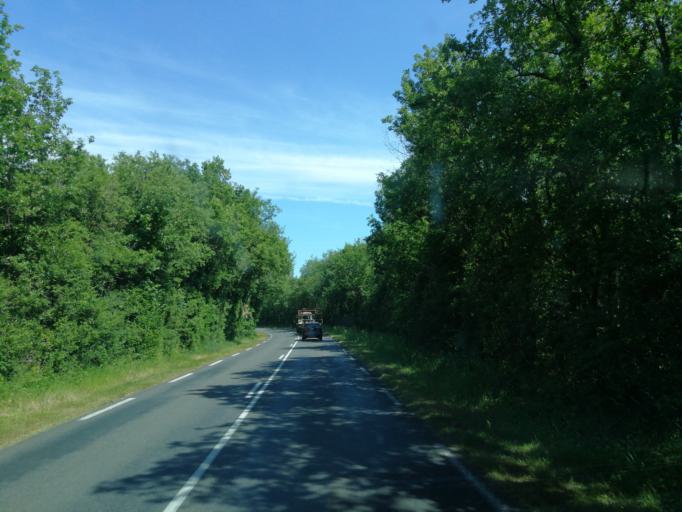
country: FR
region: Poitou-Charentes
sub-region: Departement des Deux-Sevres
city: Saint-Jean-de-Thouars
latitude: 46.9722
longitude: -0.1689
